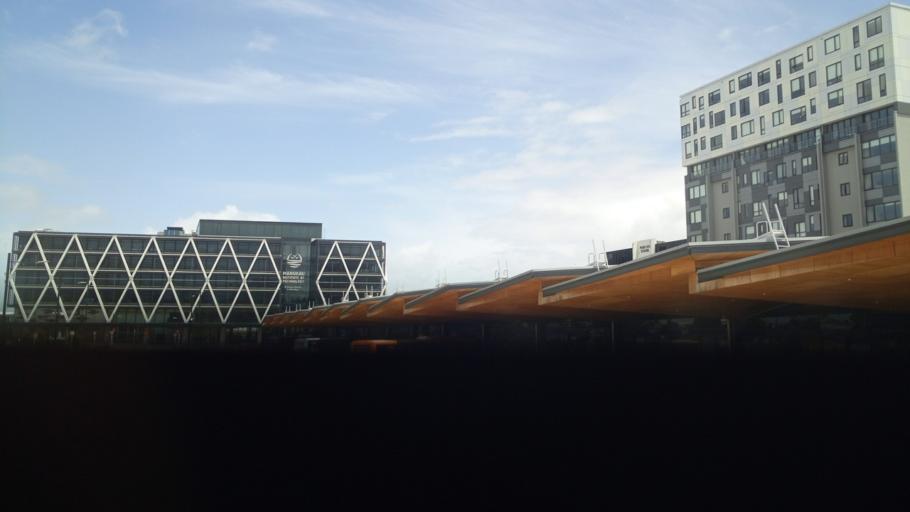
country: NZ
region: Auckland
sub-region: Auckland
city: Manukau City
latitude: -36.9935
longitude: 174.8796
